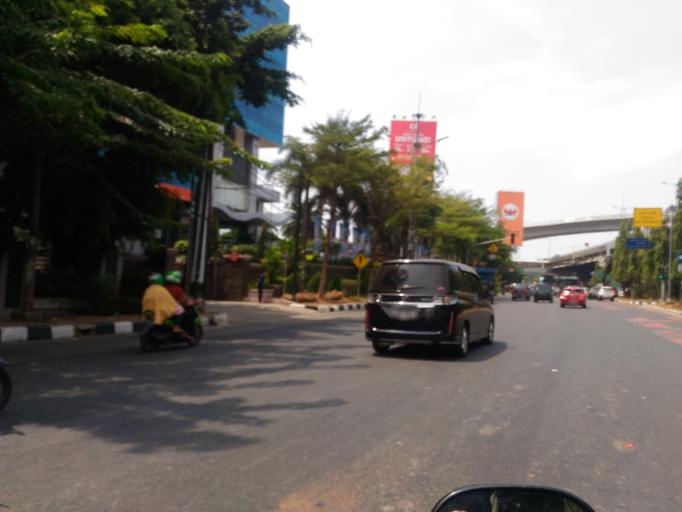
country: ID
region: Jakarta Raya
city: Jakarta
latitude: -6.2409
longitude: 106.8773
